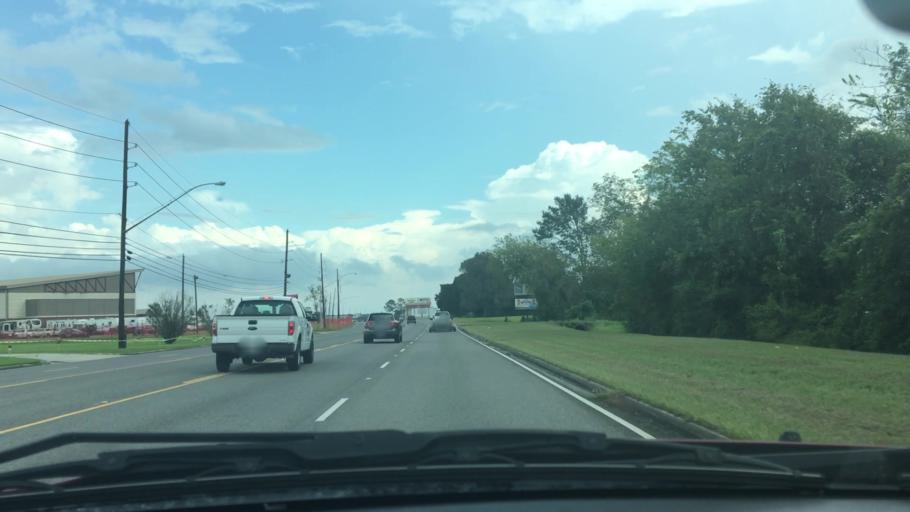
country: US
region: Louisiana
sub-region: Saint John the Baptist Parish
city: Laplace
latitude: 30.0707
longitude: -90.4771
